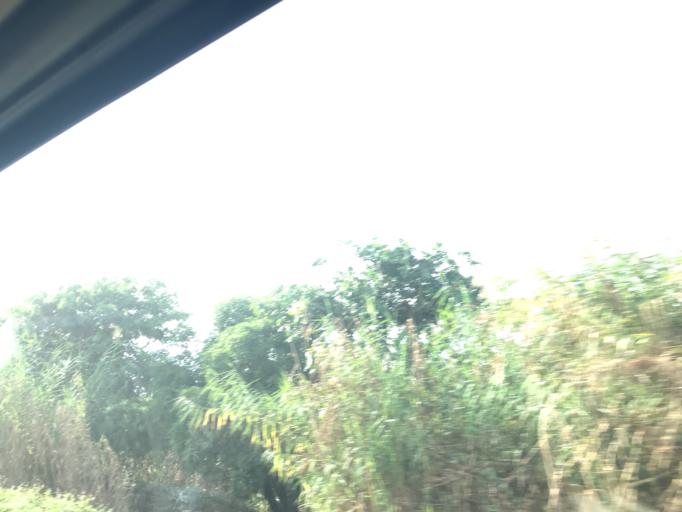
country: PE
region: Lambayeque
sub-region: Provincia de Chiclayo
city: Chongoyape
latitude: -6.6757
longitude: -79.4401
